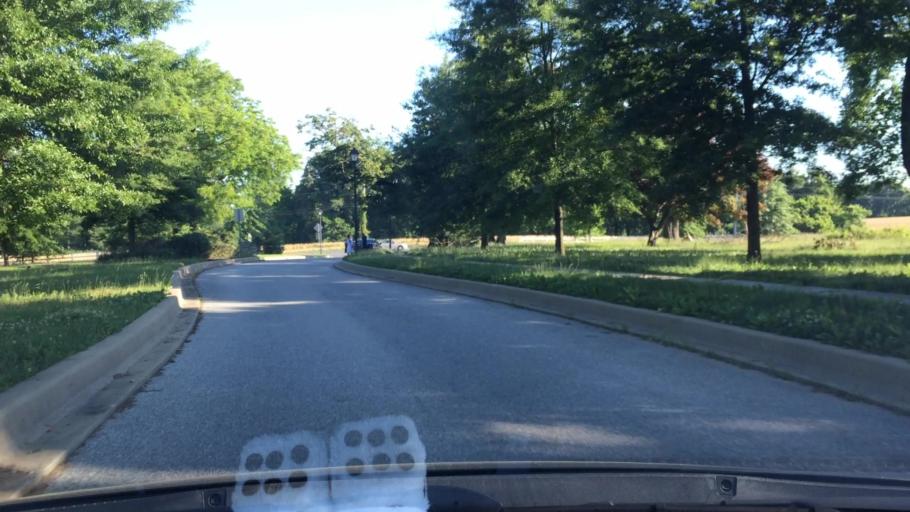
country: US
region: Delaware
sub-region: New Castle County
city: Delaware City
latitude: 39.5405
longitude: -75.6618
